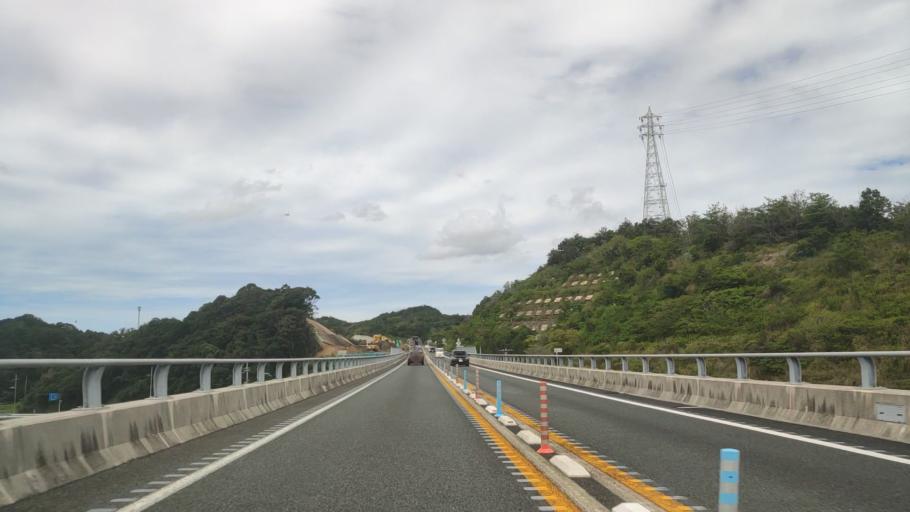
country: JP
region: Wakayama
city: Gobo
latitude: 33.8700
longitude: 135.1892
